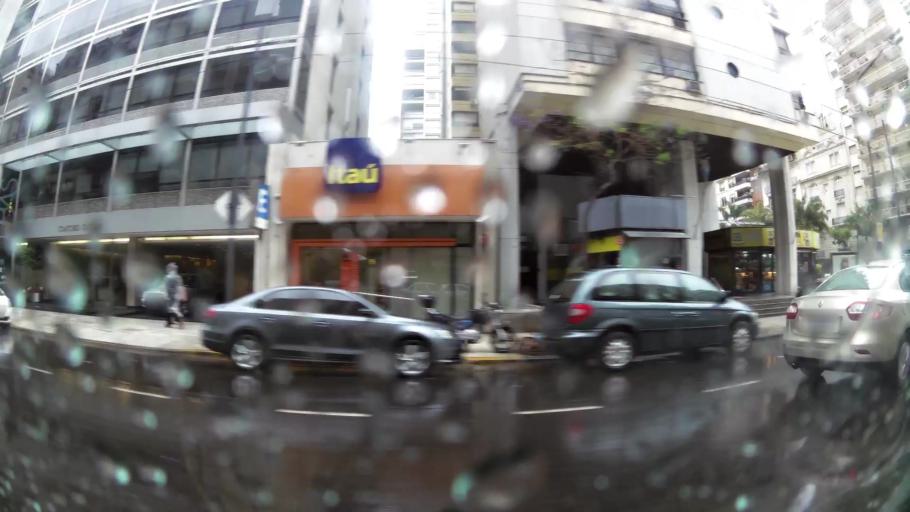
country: AR
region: Buenos Aires F.D.
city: Retiro
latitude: -34.5941
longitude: -58.3932
